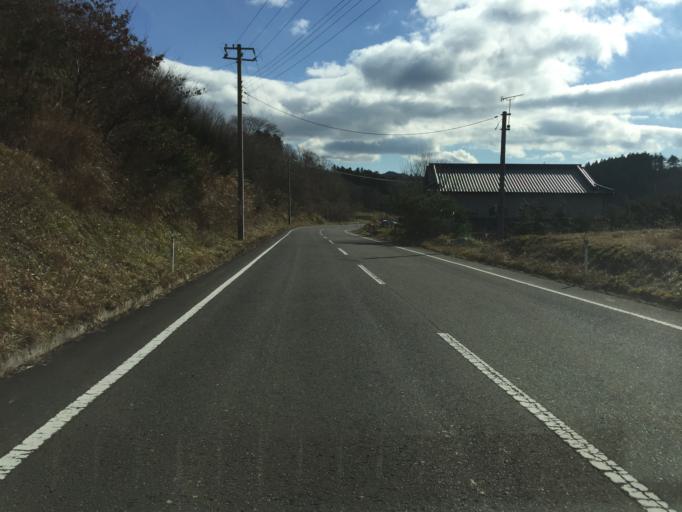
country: JP
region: Fukushima
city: Ishikawa
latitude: 37.2491
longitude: 140.5554
